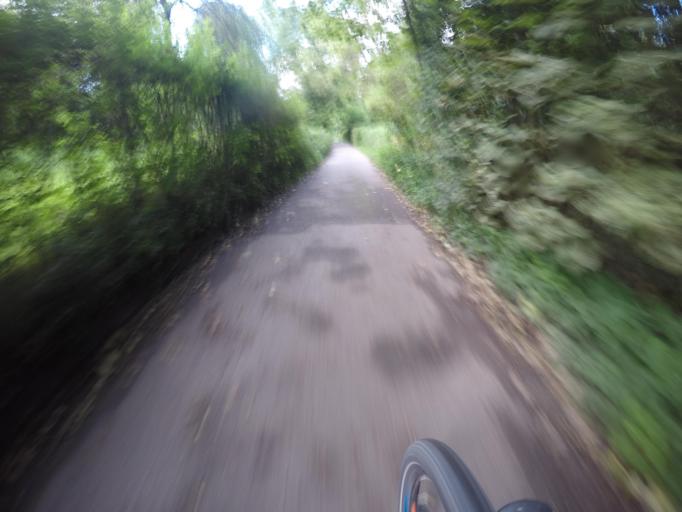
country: DE
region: Baden-Wuerttemberg
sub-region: Regierungsbezirk Stuttgart
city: Ostfildern
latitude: 48.7502
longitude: 9.2467
